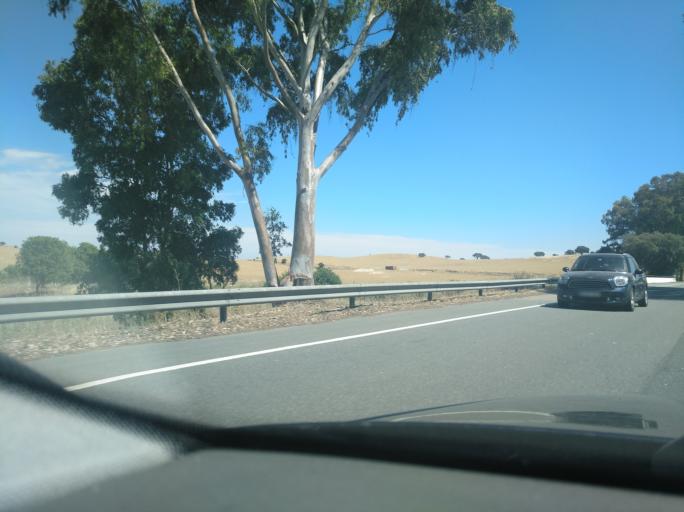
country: PT
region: Beja
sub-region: Castro Verde
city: Castro Verde
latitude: 37.6824
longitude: -8.0840
